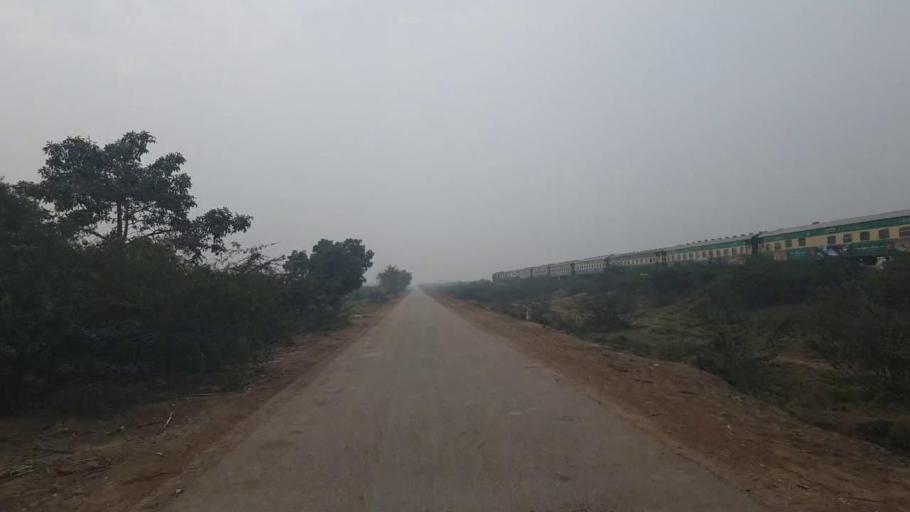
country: PK
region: Sindh
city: Tando Adam
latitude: 25.7075
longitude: 68.6430
